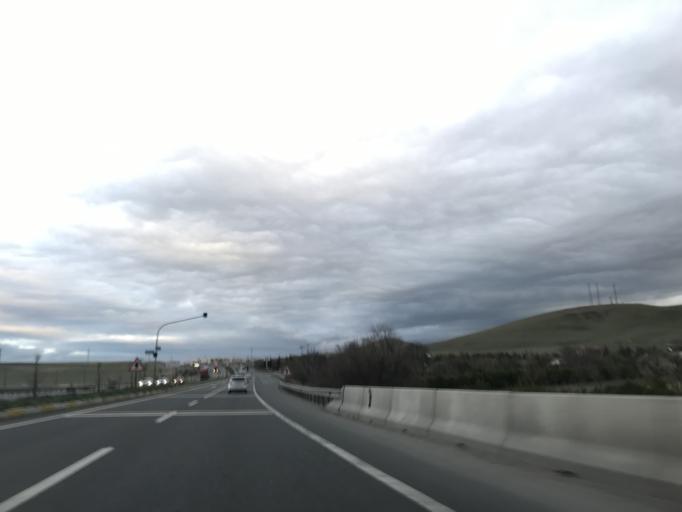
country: TR
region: Ankara
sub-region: Goelbasi
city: Golbasi
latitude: 39.6566
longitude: 32.8152
